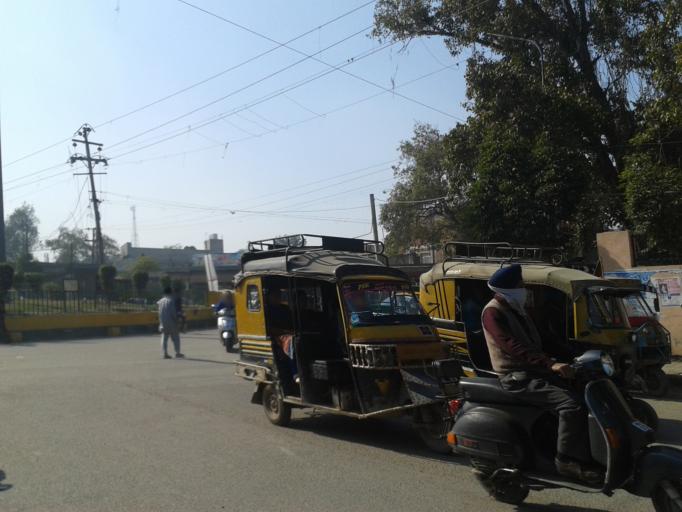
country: IN
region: Punjab
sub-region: Amritsar
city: Amritsar
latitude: 31.6284
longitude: 74.8703
